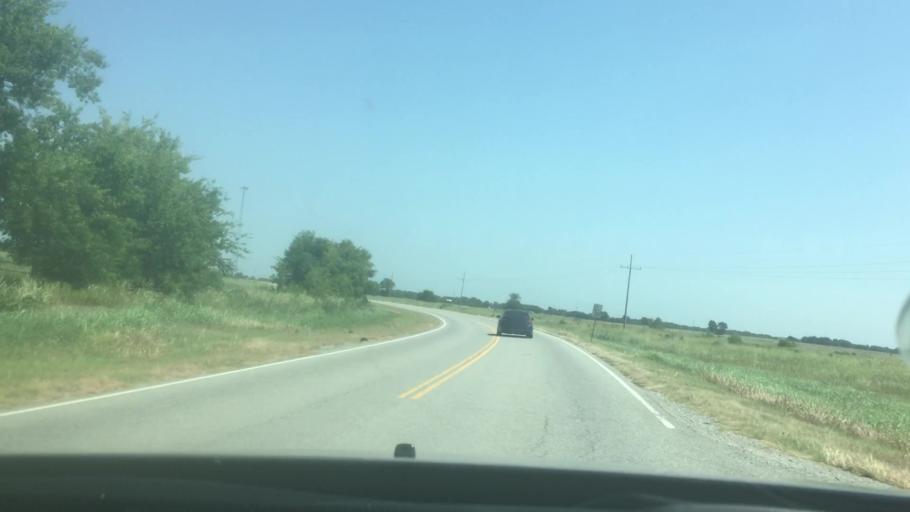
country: US
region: Oklahoma
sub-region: Coal County
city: Coalgate
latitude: 34.5006
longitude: -96.4074
